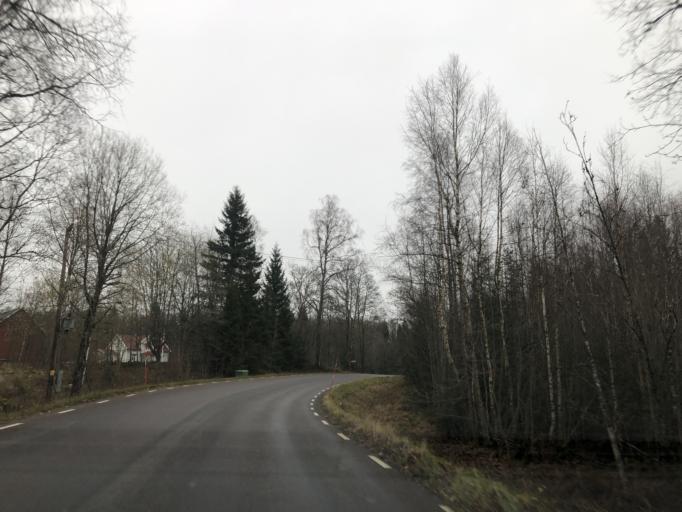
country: SE
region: Vaestra Goetaland
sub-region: Ulricehamns Kommun
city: Ulricehamn
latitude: 57.7653
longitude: 13.4685
